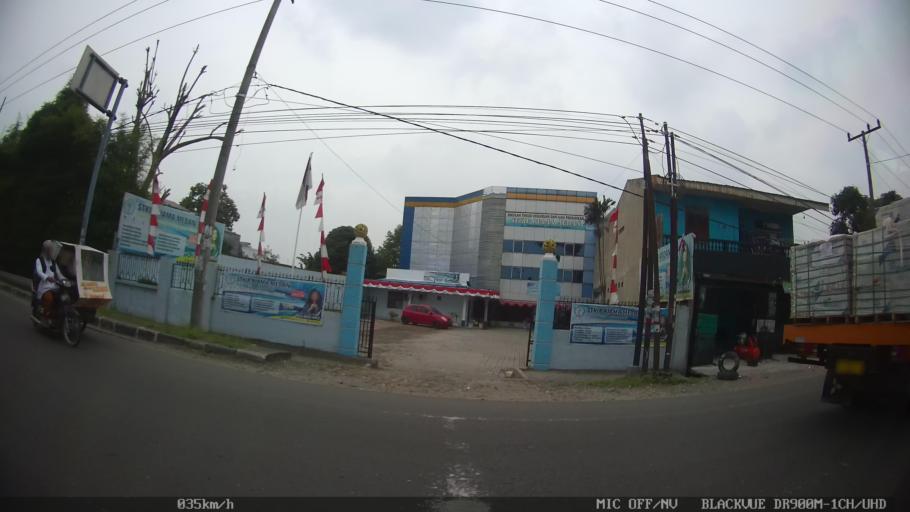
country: ID
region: North Sumatra
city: Deli Tua
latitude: 3.5382
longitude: 98.6967
